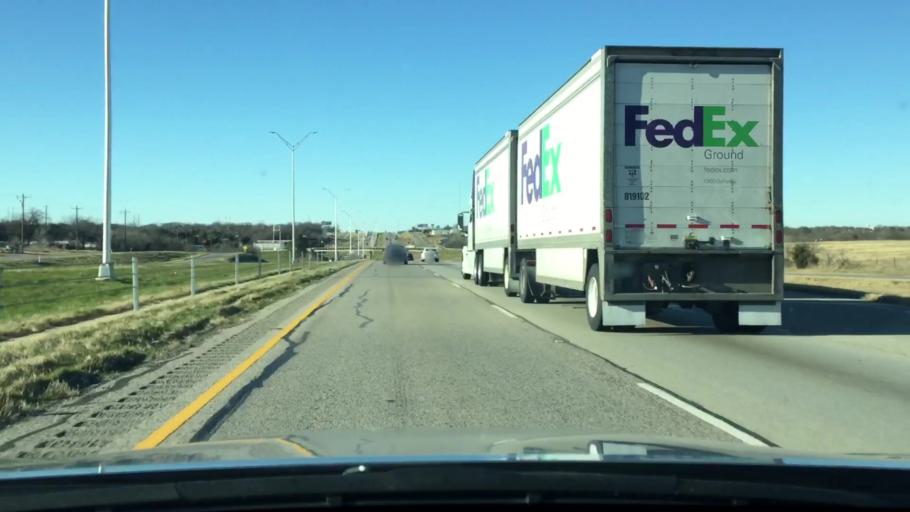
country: US
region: Texas
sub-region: Johnson County
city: Alvarado
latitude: 32.4609
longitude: -97.2637
